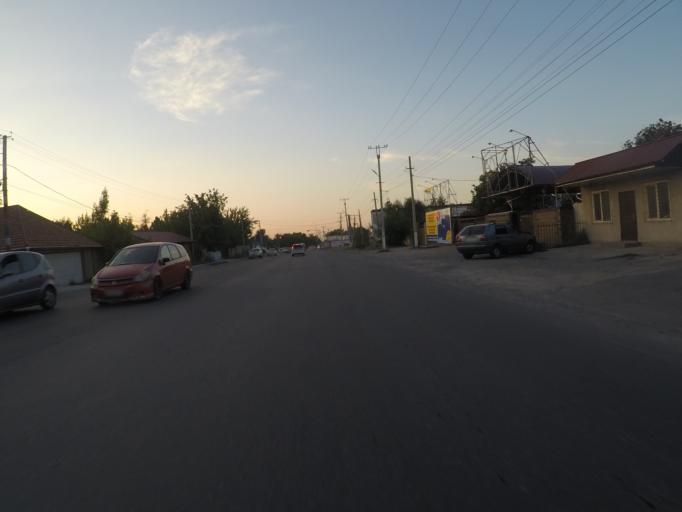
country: KG
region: Chuy
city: Lebedinovka
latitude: 42.8111
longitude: 74.6459
